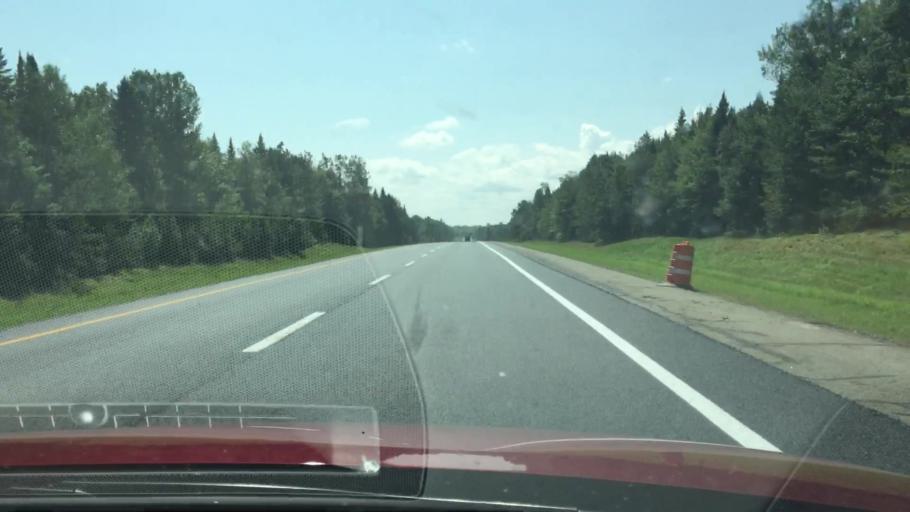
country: US
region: Maine
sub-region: Penobscot County
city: Patten
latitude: 45.8561
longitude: -68.4244
